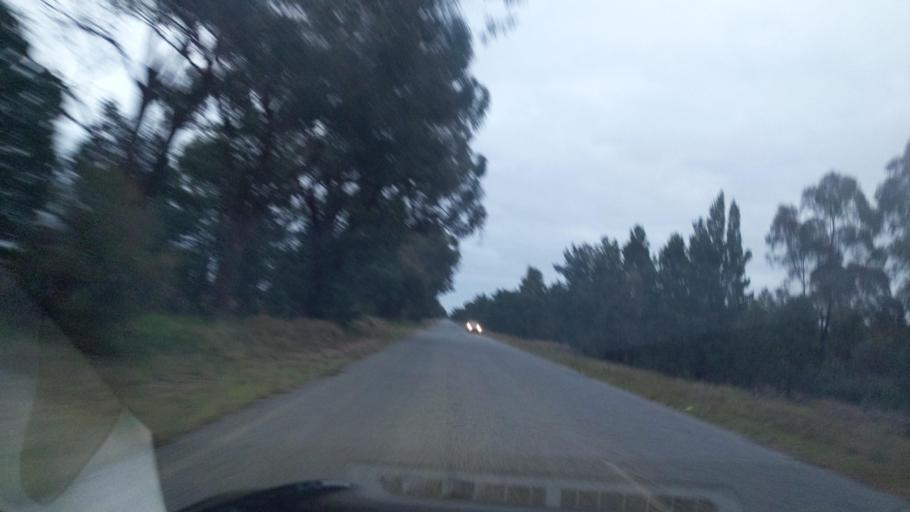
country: AU
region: New South Wales
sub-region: Narrandera
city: Narrandera
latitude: -34.7518
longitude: 146.8414
